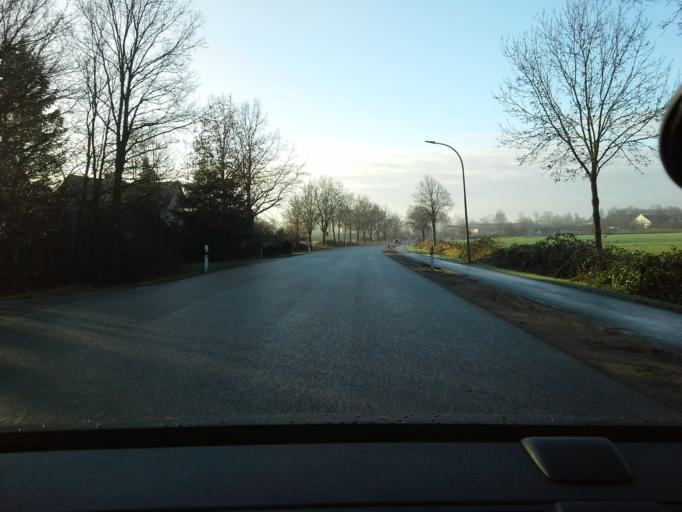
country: DE
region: Schleswig-Holstein
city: Borstel-Hohenraden
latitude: 53.6930
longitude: 9.8197
